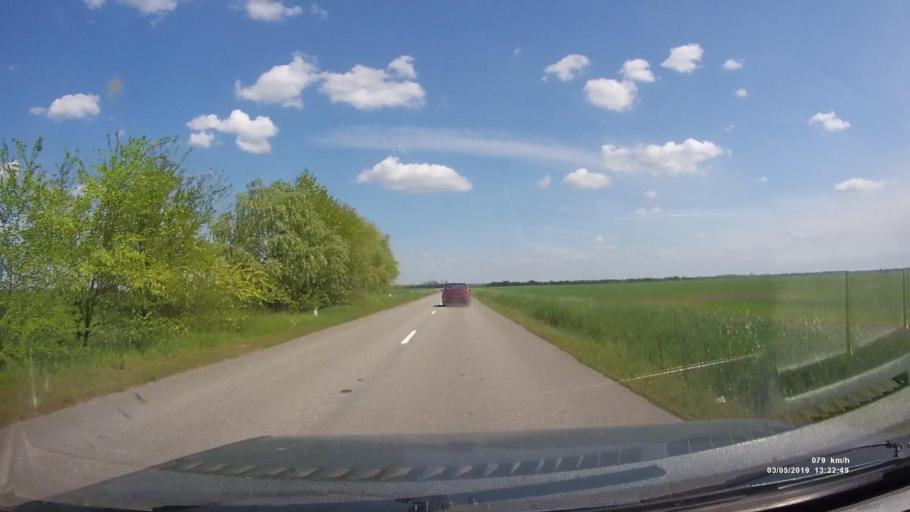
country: RU
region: Rostov
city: Semikarakorsk
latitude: 47.5625
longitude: 40.7707
